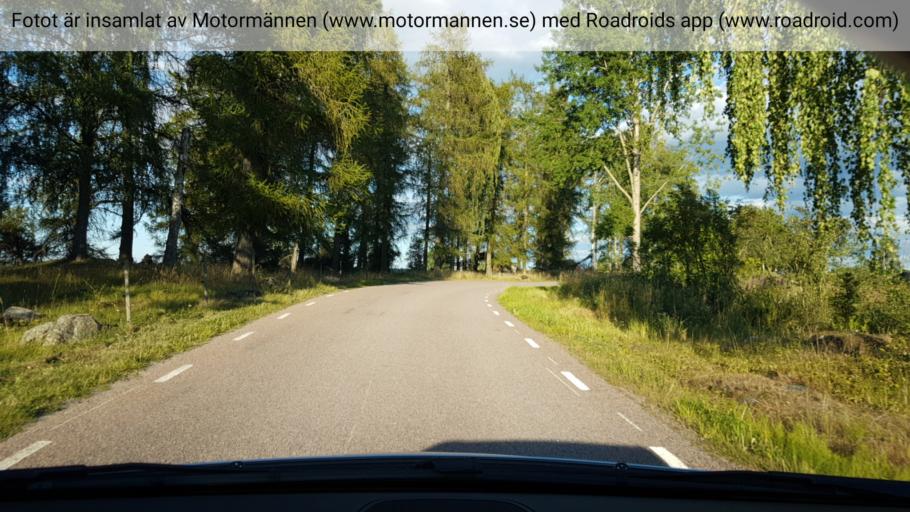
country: SE
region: Vaestmanland
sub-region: Vasteras
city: Tillberga
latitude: 59.6919
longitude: 16.6777
